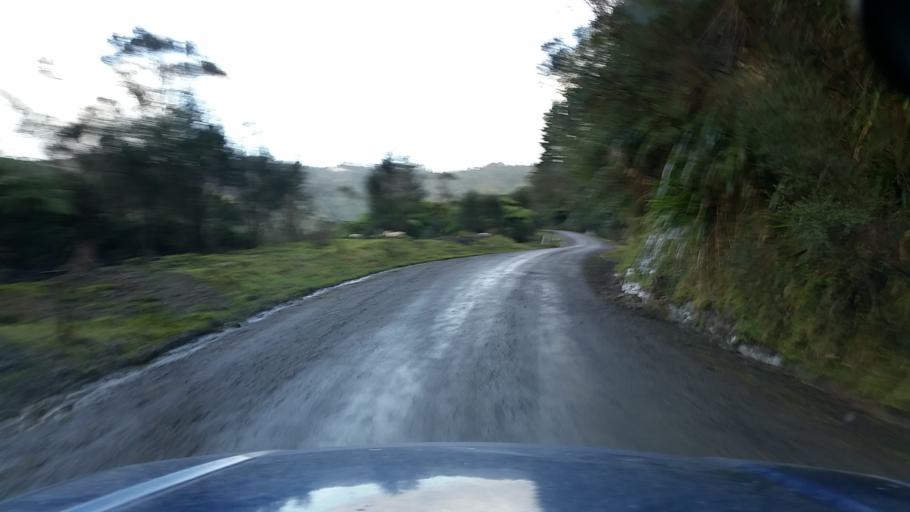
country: NZ
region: Taranaki
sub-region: South Taranaki District
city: Patea
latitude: -39.5565
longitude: 174.5736
